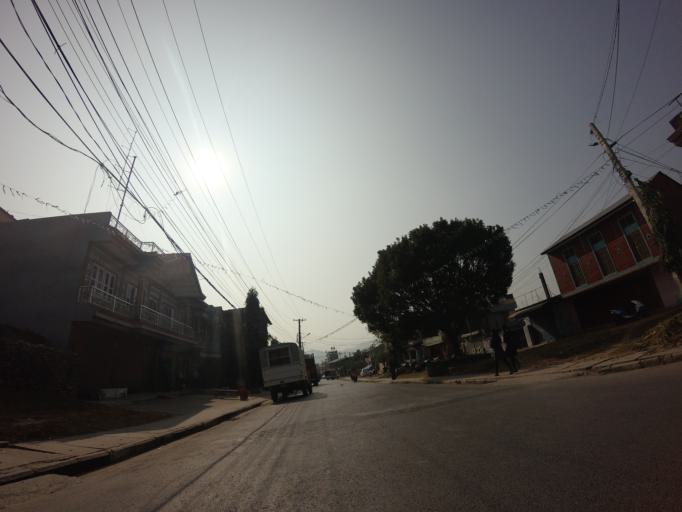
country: NP
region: Western Region
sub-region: Gandaki Zone
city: Pokhara
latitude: 28.2138
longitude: 83.9818
